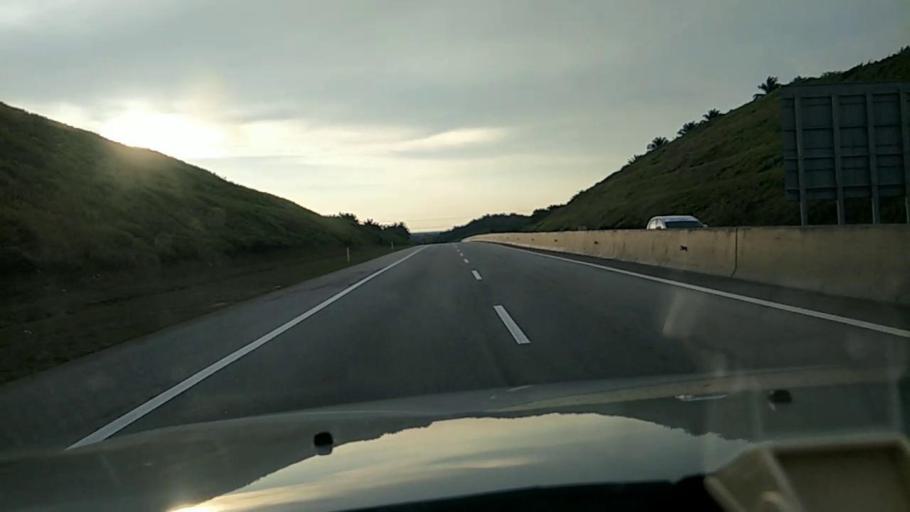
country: MY
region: Selangor
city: Batu Arang
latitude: 3.2836
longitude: 101.4431
